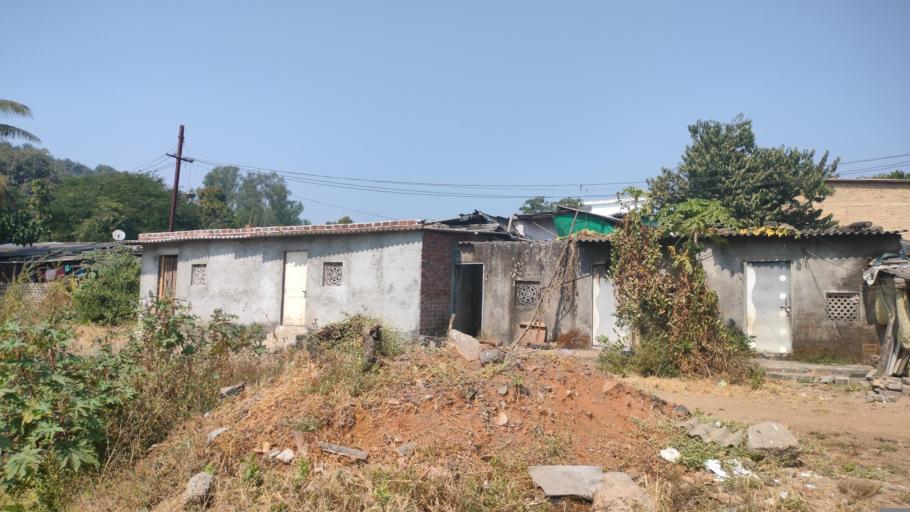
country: IN
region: Maharashtra
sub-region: Thane
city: Bhayandar
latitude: 19.3575
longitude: 72.9008
